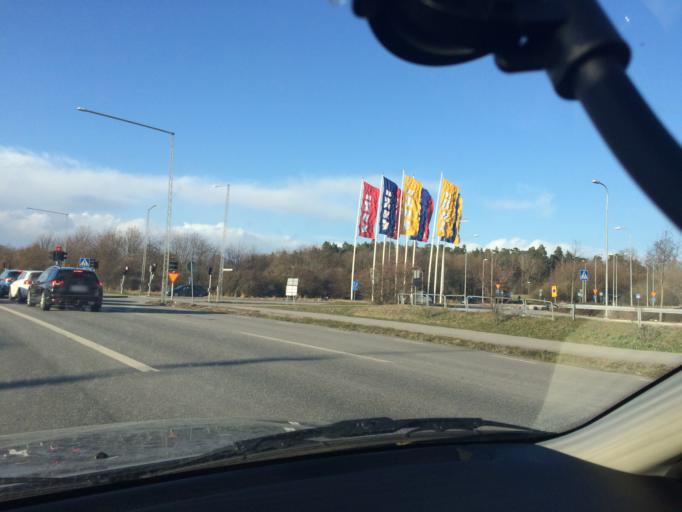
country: SE
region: Stockholm
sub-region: Jarfalla Kommun
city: Jakobsberg
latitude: 59.4219
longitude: 17.8554
